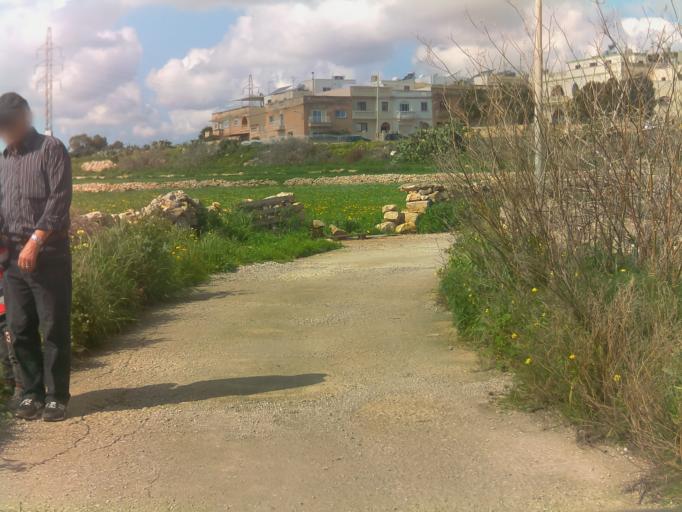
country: MT
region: Saint Lucia
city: Santa Lucija
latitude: 35.8595
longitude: 14.5010
